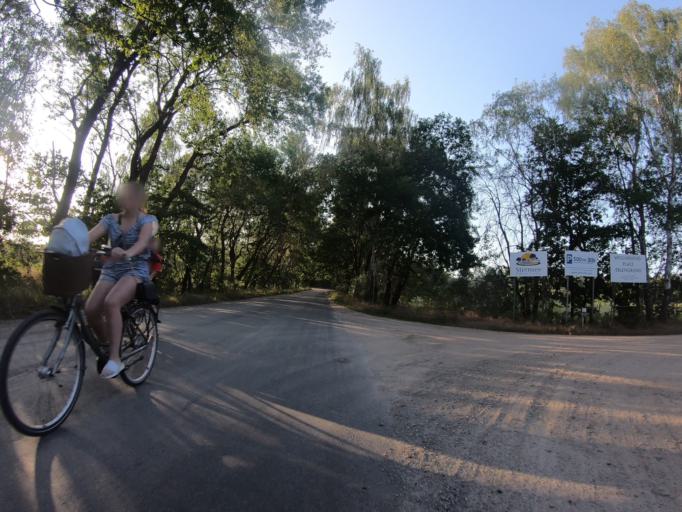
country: DE
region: Lower Saxony
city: Wagenhoff
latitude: 52.5211
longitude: 10.4790
